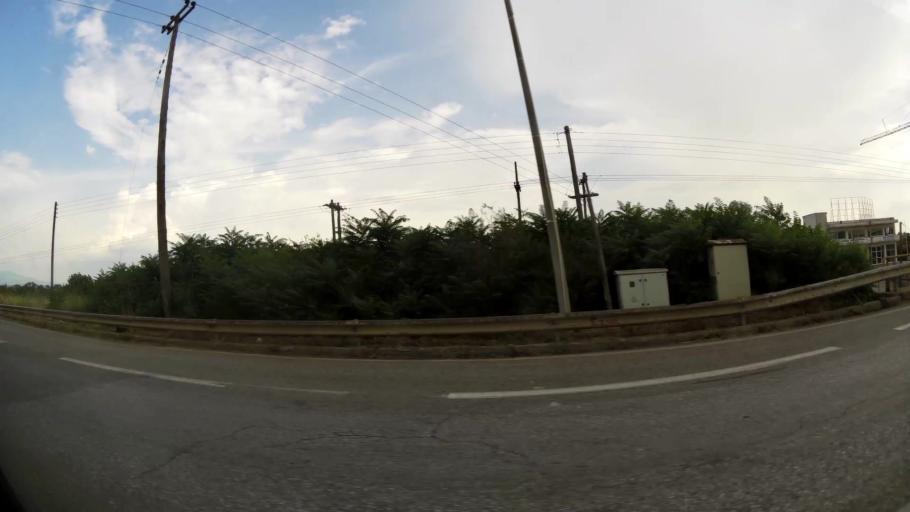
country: GR
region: Central Macedonia
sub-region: Nomos Thessalonikis
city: Sindos
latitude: 40.6520
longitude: 22.8281
